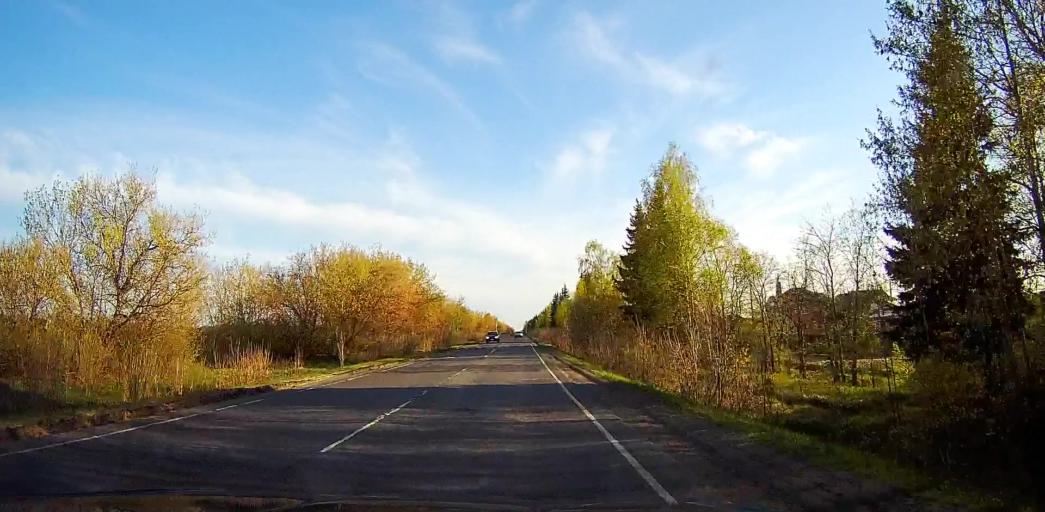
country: RU
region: Moskovskaya
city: Bronnitsy
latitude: 55.3186
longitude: 38.2172
